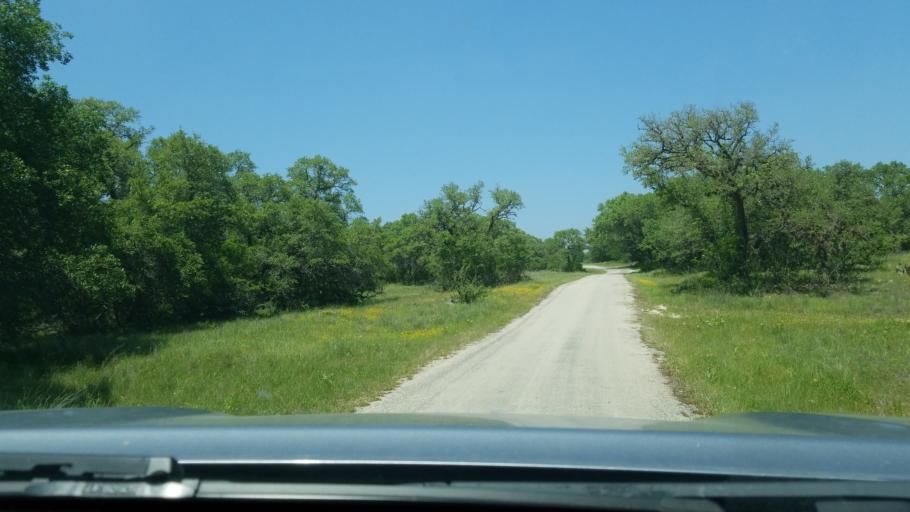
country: US
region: Texas
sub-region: Blanco County
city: Blanco
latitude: 30.0198
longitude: -98.4607
